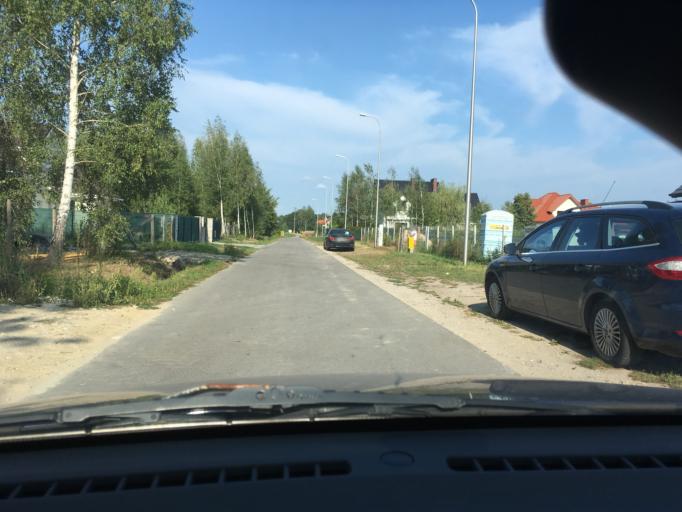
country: PL
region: Masovian Voivodeship
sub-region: Powiat piaseczynski
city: Lesznowola
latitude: 52.0516
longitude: 20.9368
